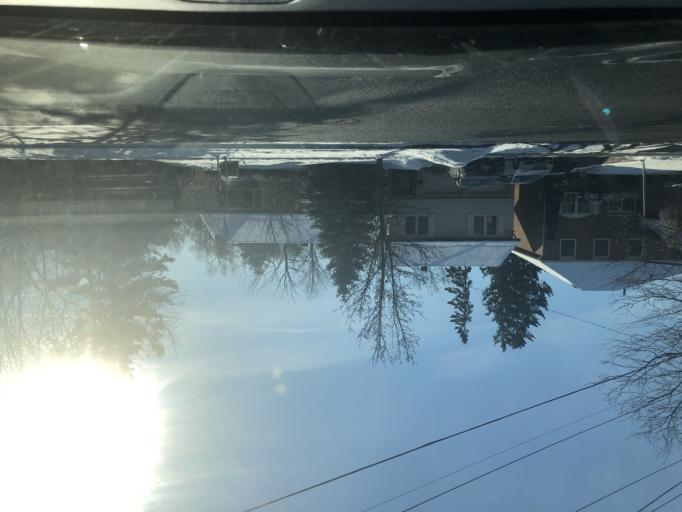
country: CA
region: Ontario
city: Scarborough
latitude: 43.7869
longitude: -79.1539
